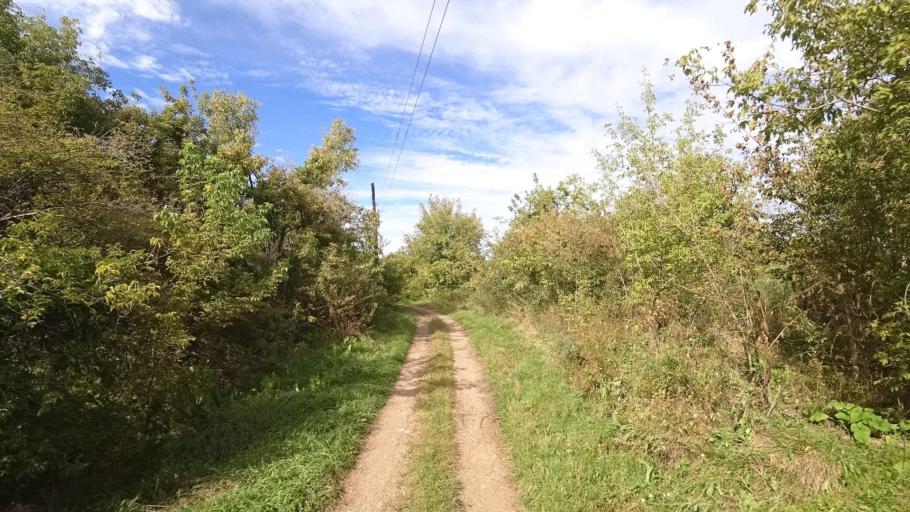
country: RU
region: Primorskiy
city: Dostoyevka
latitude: 44.3264
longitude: 133.4847
